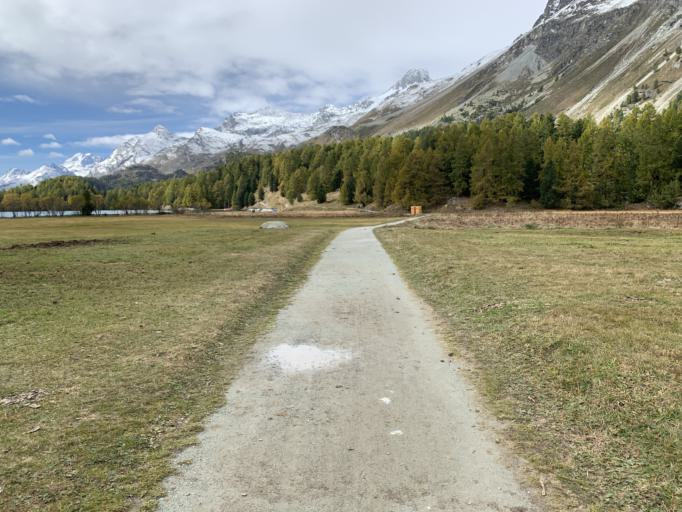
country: CH
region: Grisons
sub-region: Maloja District
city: Silvaplana
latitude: 46.4290
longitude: 9.7543
